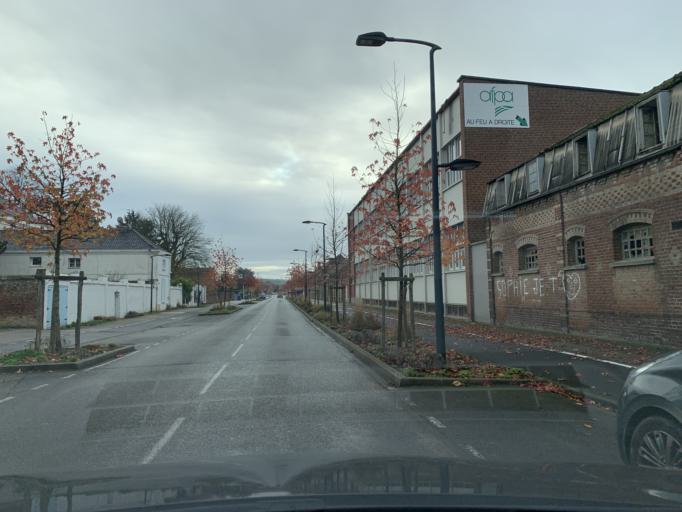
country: FR
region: Nord-Pas-de-Calais
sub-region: Departement du Nord
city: Cantin
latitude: 50.3150
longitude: 3.1208
